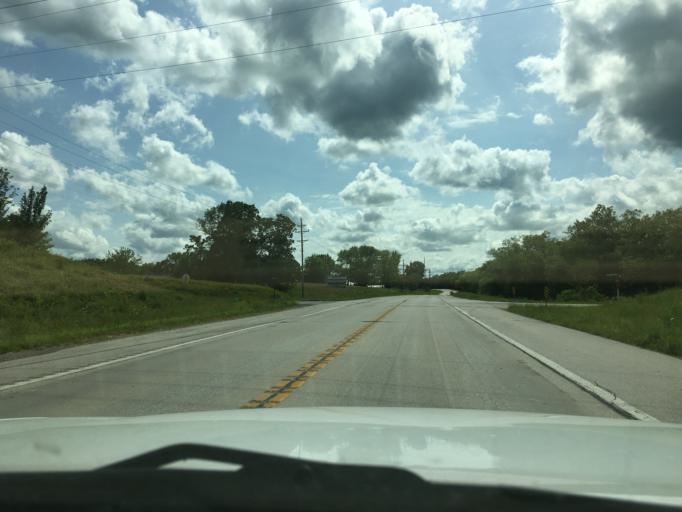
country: US
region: Missouri
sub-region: Franklin County
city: Gerald
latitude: 38.4118
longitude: -91.3109
